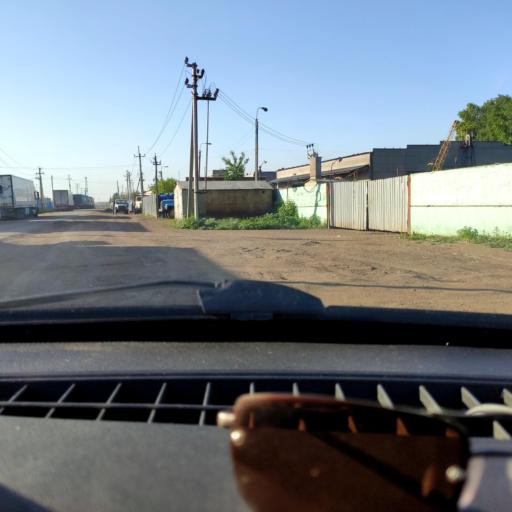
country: RU
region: Bashkortostan
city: Ufa
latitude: 54.5695
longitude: 55.9254
